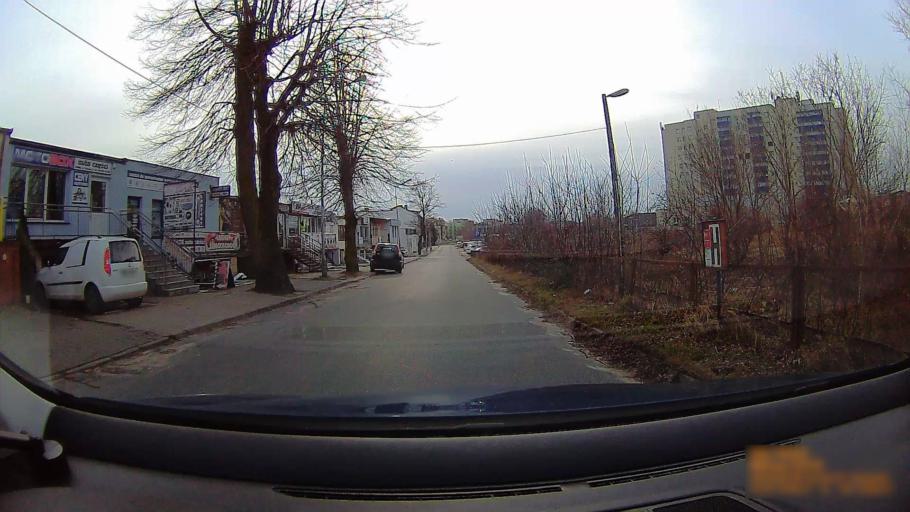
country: PL
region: Greater Poland Voivodeship
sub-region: Konin
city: Konin
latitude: 52.2322
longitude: 18.2626
